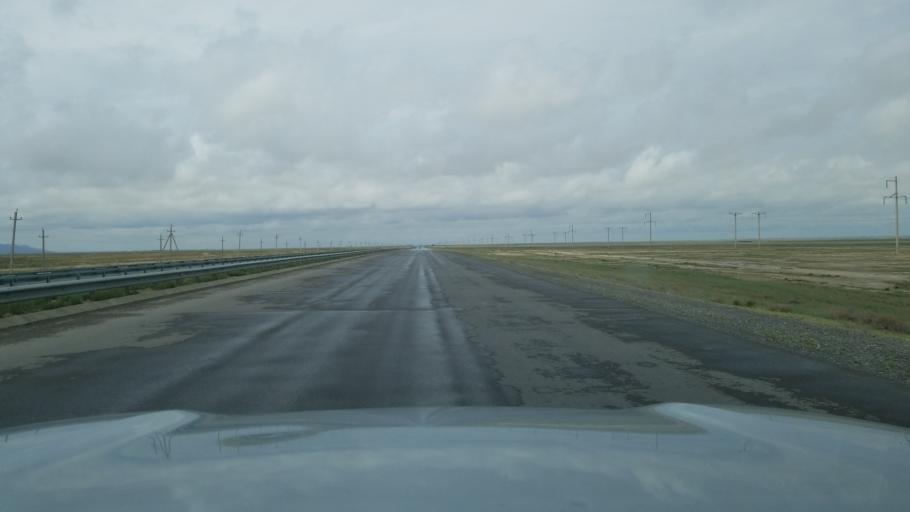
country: TM
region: Balkan
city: Gazanjyk
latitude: 39.1950
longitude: 55.7796
